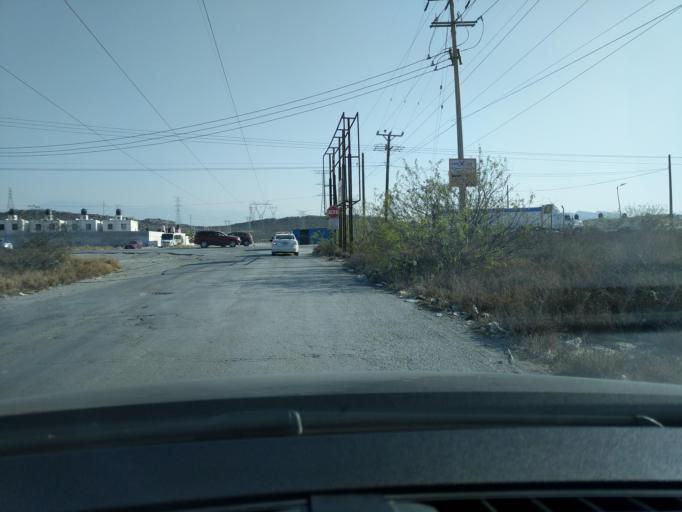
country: MX
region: Coahuila
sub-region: Ramos Arizpe
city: Ramos Arizpe
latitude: 25.5354
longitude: -100.9781
